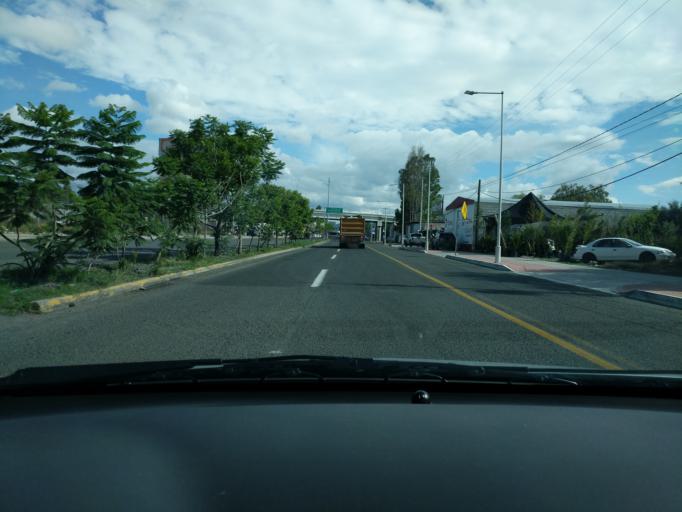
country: MX
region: Queretaro
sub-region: El Marques
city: Hacienda la Cruz [Fraccionamiento]
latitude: 20.6382
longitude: -100.2600
